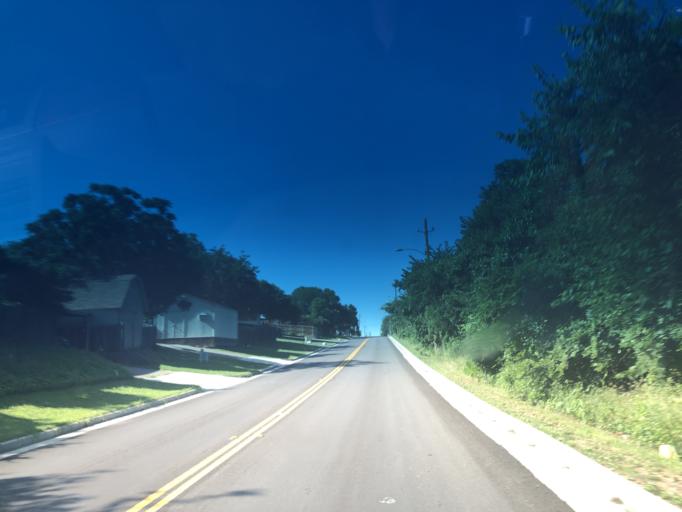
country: US
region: Texas
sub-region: Dallas County
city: Grand Prairie
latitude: 32.7185
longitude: -97.0197
